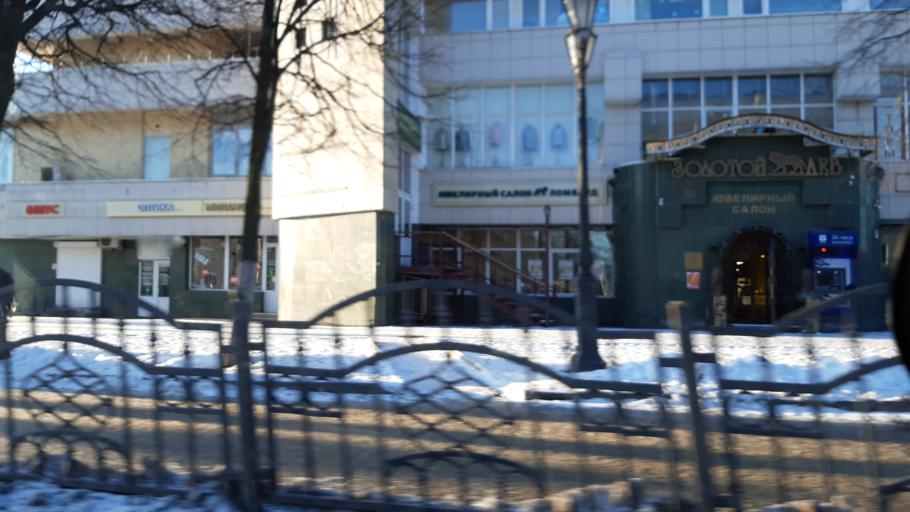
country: RU
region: Moskovskaya
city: Sergiyev Posad
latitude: 56.3162
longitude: 38.1374
